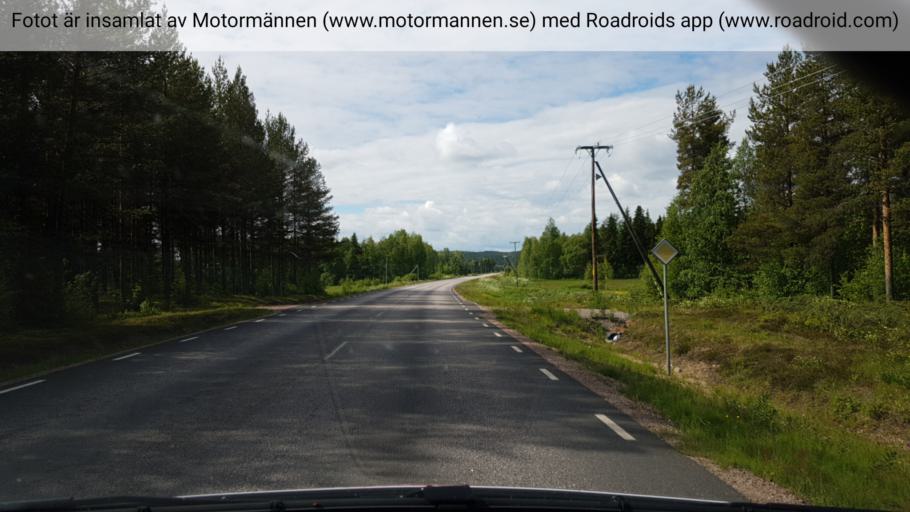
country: SE
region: Norrbotten
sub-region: Overtornea Kommun
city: OEvertornea
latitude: 66.4692
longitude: 23.6669
